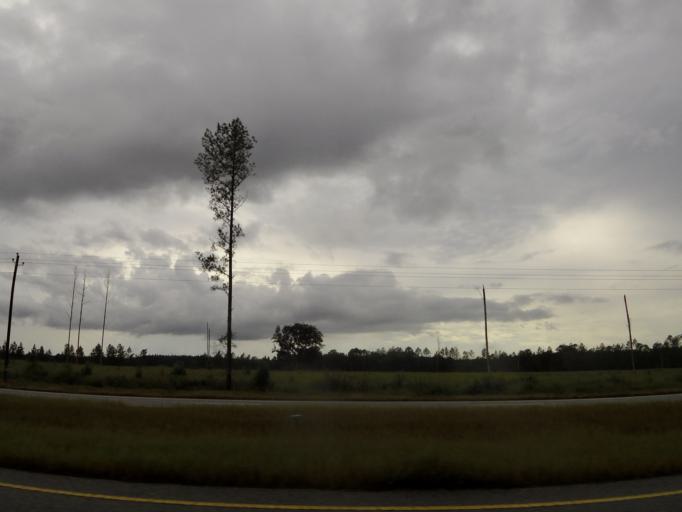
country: US
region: Georgia
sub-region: Wayne County
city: Jesup
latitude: 31.5462
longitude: -81.8076
